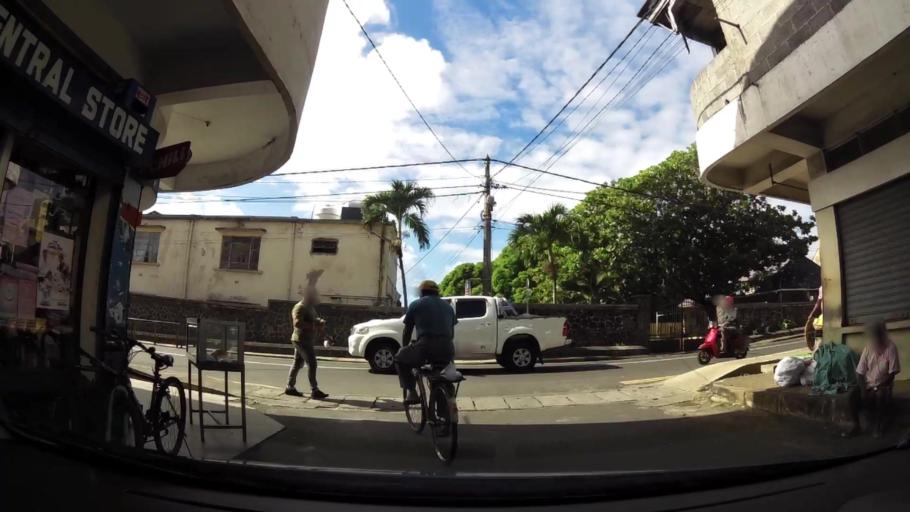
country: MU
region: Grand Port
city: Mahebourg
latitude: -20.4115
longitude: 57.7058
